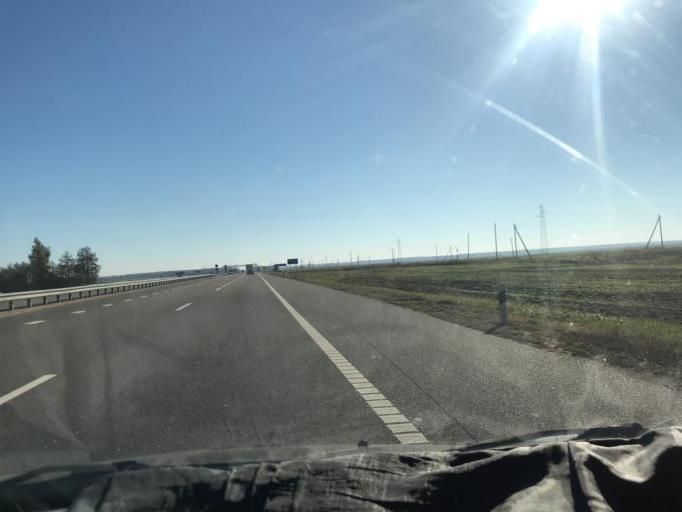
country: BY
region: Mogilev
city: Yalizava
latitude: 53.2355
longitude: 28.9731
